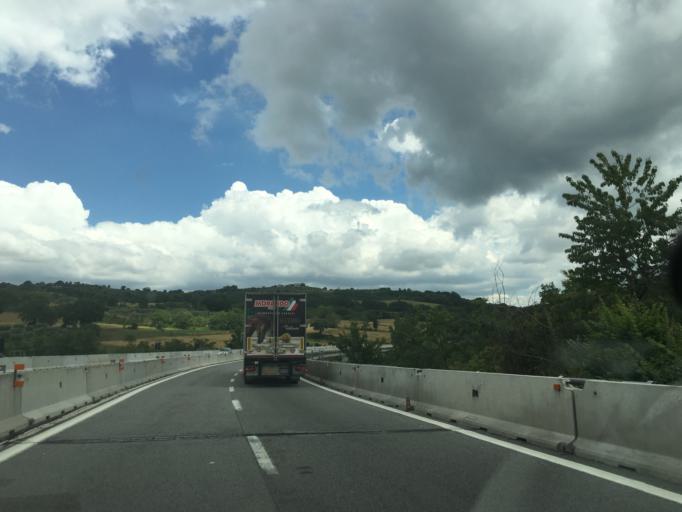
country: IT
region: Campania
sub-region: Provincia di Avellino
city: Bonito
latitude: 41.0730
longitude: 14.9968
